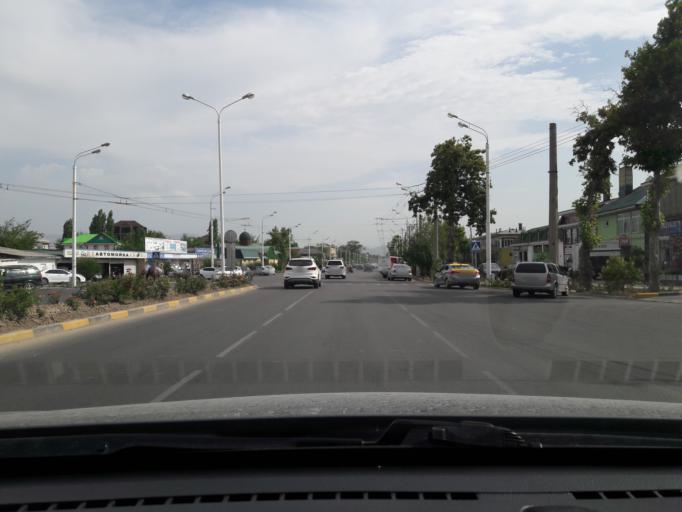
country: TJ
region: Dushanbe
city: Dushanbe
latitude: 38.5396
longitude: 68.7549
